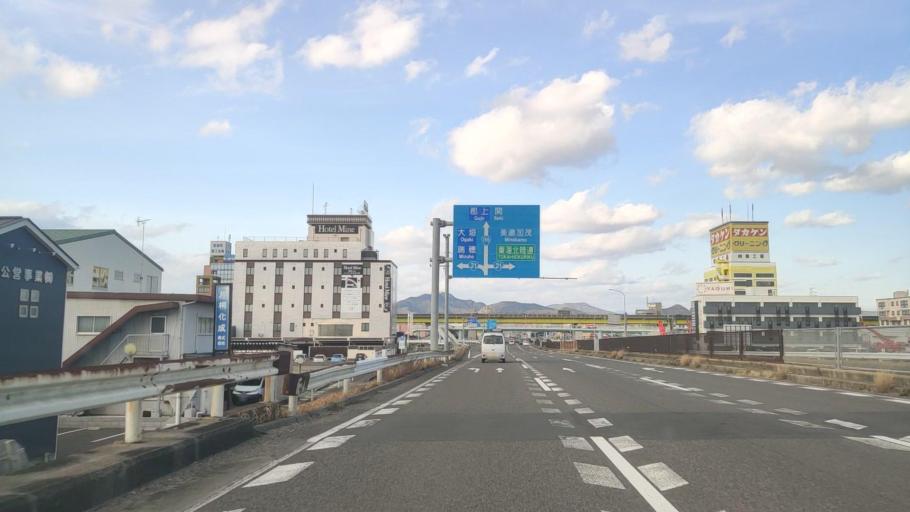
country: JP
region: Gifu
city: Kasamatsucho
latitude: 35.3854
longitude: 136.7846
